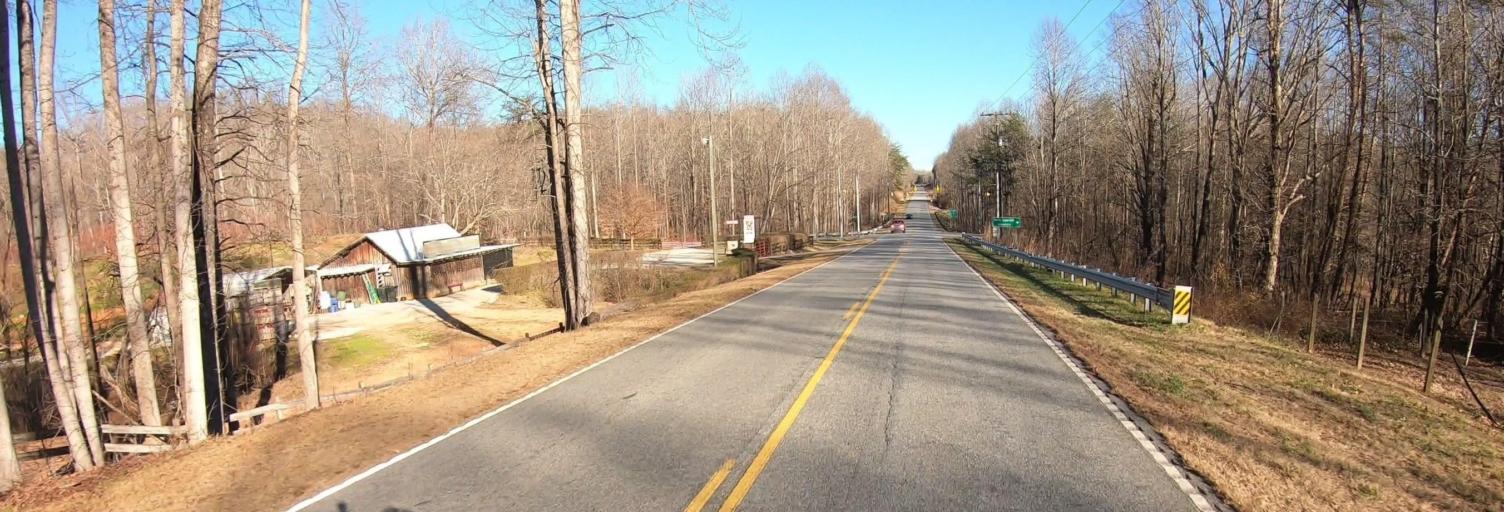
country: US
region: South Carolina
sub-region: Greenville County
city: Tigerville
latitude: 35.1041
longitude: -82.3731
